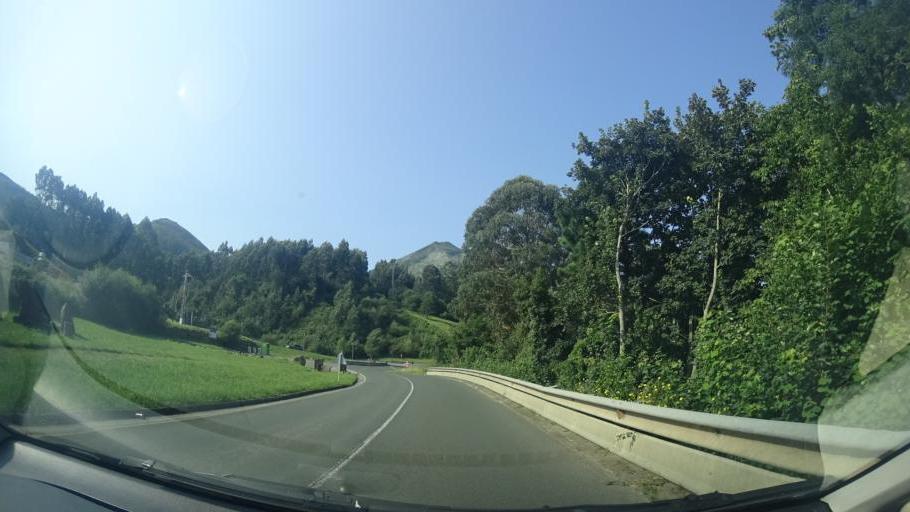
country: ES
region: Asturias
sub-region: Province of Asturias
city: Colunga
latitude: 43.4631
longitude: -5.1996
